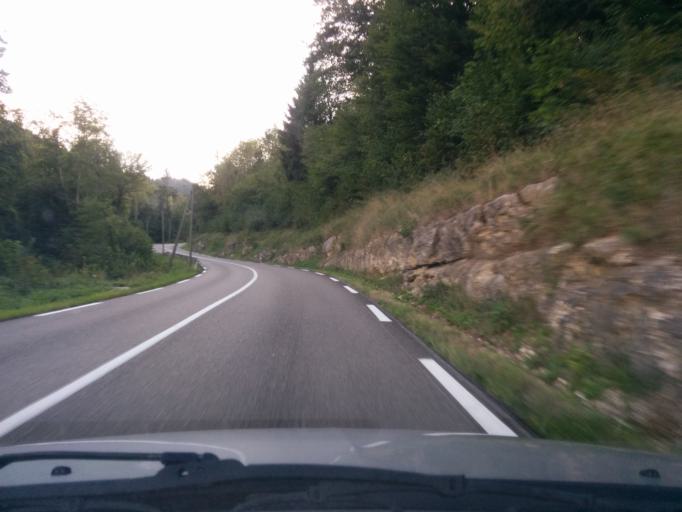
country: FR
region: Rhone-Alpes
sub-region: Departement de l'Isere
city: Saint-Aupre
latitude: 45.3468
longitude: 5.6679
